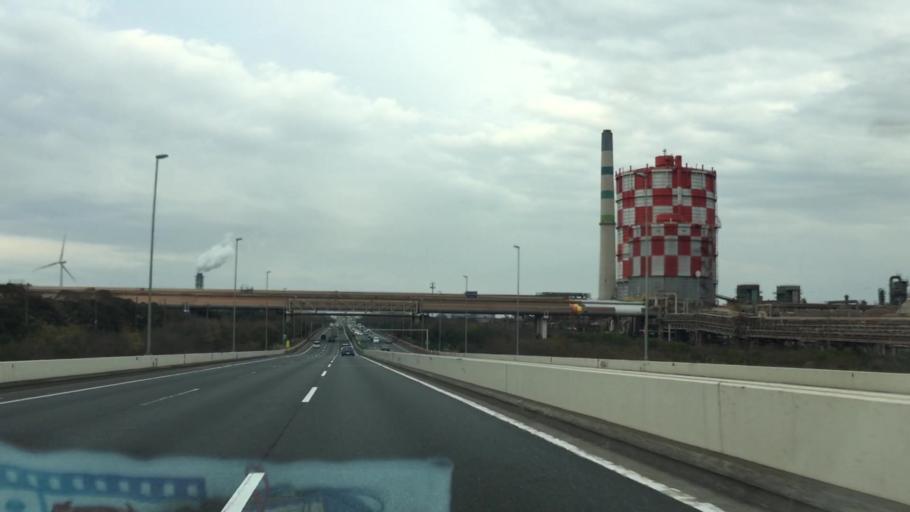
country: JP
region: Kanagawa
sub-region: Kawasaki-shi
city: Kawasaki
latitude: 35.4816
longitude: 139.7199
